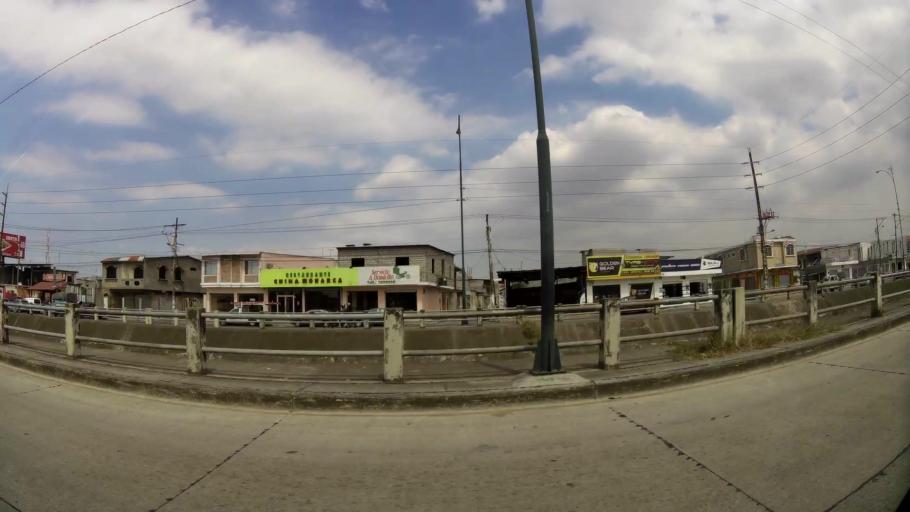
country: EC
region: Guayas
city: Eloy Alfaro
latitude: -2.0853
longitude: -79.9211
